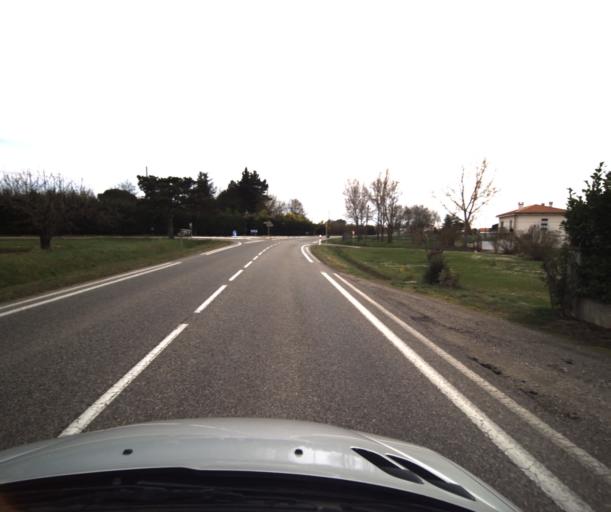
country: FR
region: Midi-Pyrenees
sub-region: Departement du Tarn-et-Garonne
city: Montbeton
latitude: 44.0712
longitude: 1.2860
